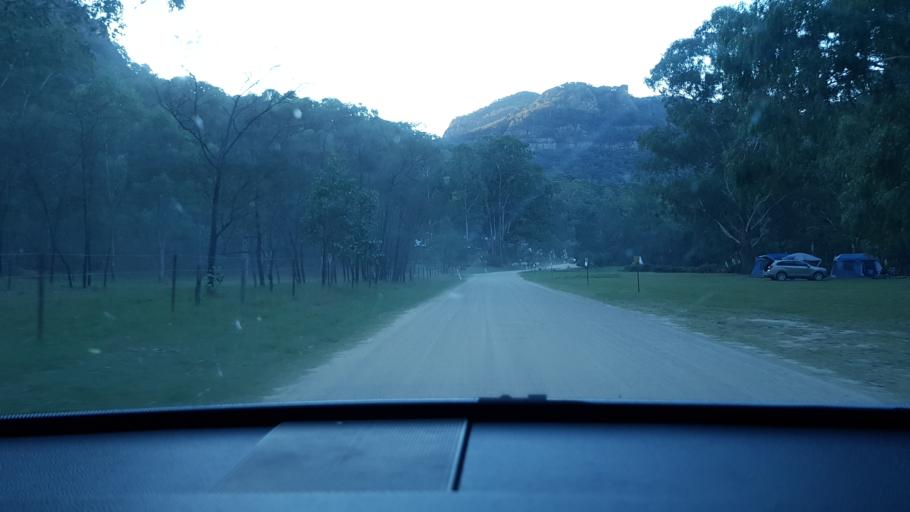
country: AU
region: New South Wales
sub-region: Lithgow
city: Portland
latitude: -33.1810
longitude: 150.2365
